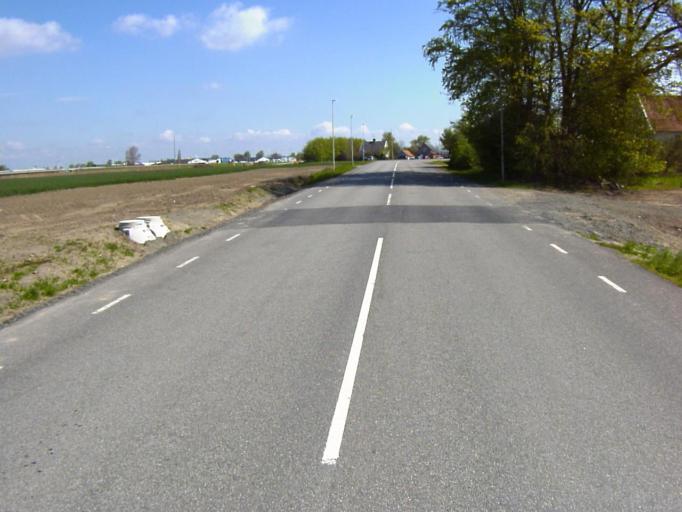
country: SE
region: Skane
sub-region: Kristianstads Kommun
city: Kristianstad
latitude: 56.0224
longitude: 14.2100
